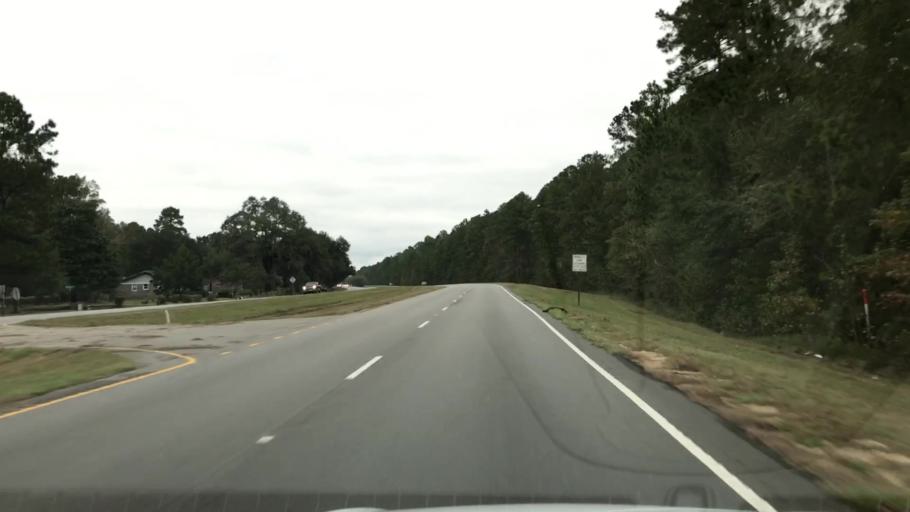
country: US
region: South Carolina
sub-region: Georgetown County
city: Georgetown
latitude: 33.2302
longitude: -79.3764
